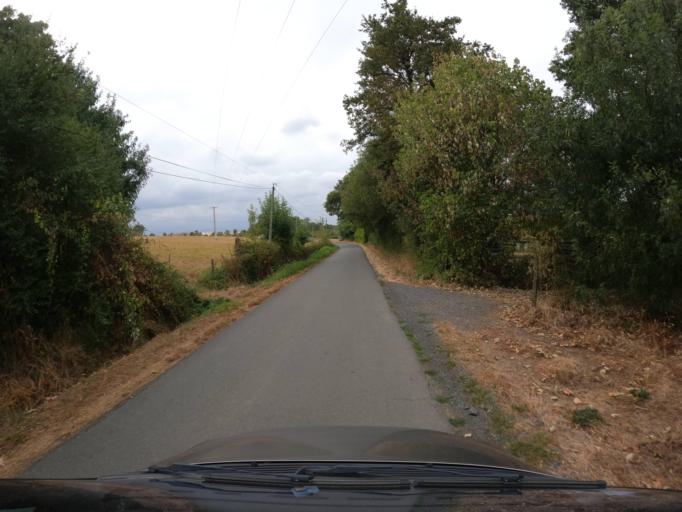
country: FR
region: Pays de la Loire
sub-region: Departement de Maine-et-Loire
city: La Romagne
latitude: 47.0545
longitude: -1.0100
